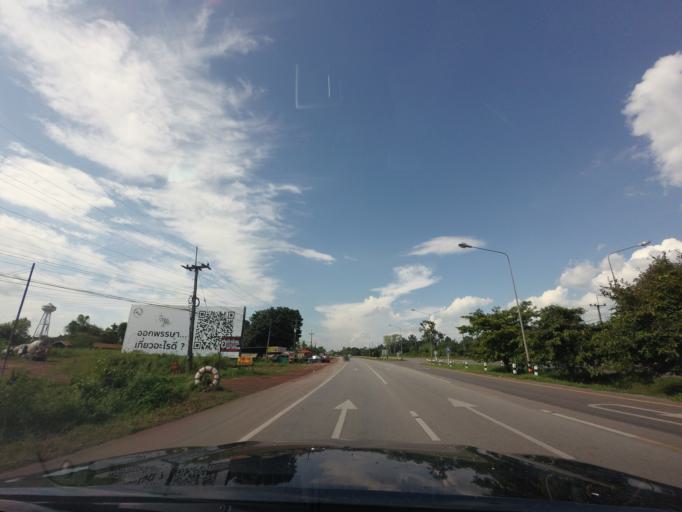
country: TH
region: Nong Khai
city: Sa Khrai
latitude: 17.6697
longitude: 102.7907
